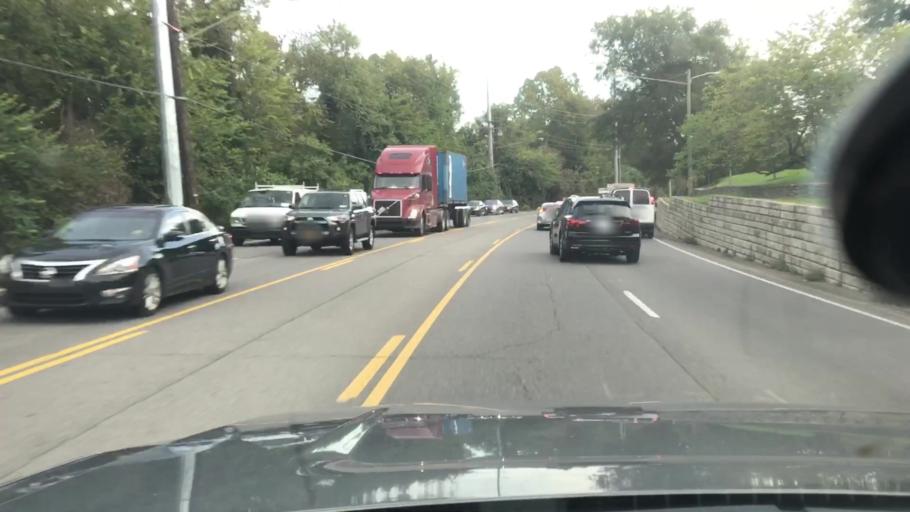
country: US
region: Tennessee
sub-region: Davidson County
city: Oak Hill
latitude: 36.1170
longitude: -86.8104
